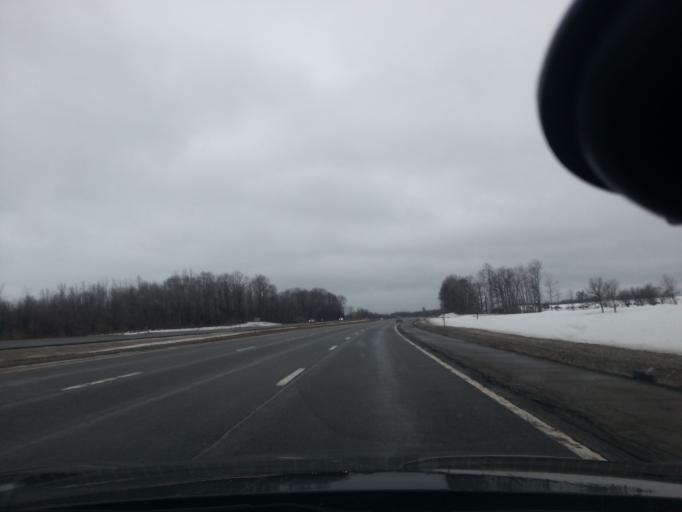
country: US
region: New York
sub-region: Onondaga County
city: Brewerton
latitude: 43.2563
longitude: -76.1311
